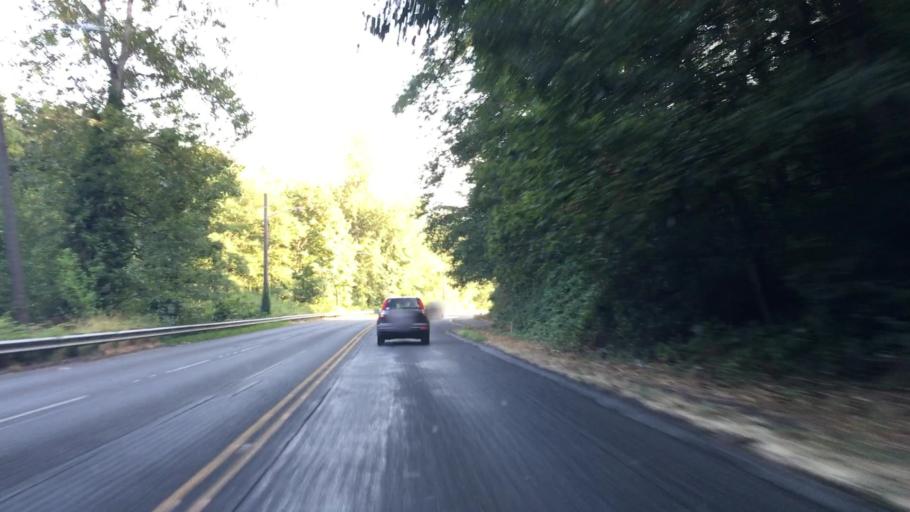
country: US
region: Washington
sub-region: Pierce County
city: Fife Heights
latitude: 47.2795
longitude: -122.3672
